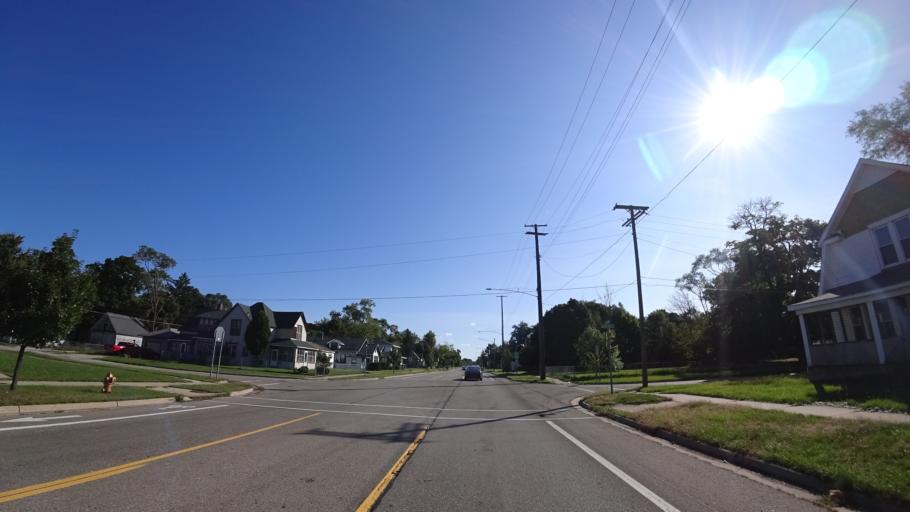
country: US
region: Michigan
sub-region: Berrien County
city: Benton Harbor
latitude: 42.1178
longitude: -86.4445
